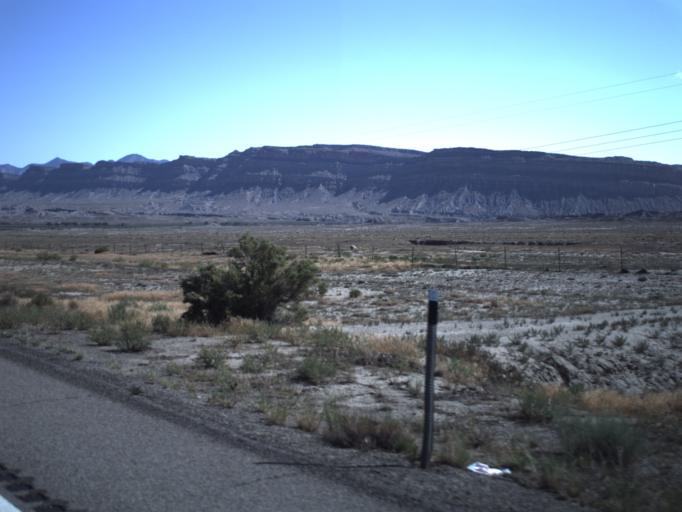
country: US
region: Utah
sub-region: Carbon County
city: East Carbon City
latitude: 39.2272
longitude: -110.3387
